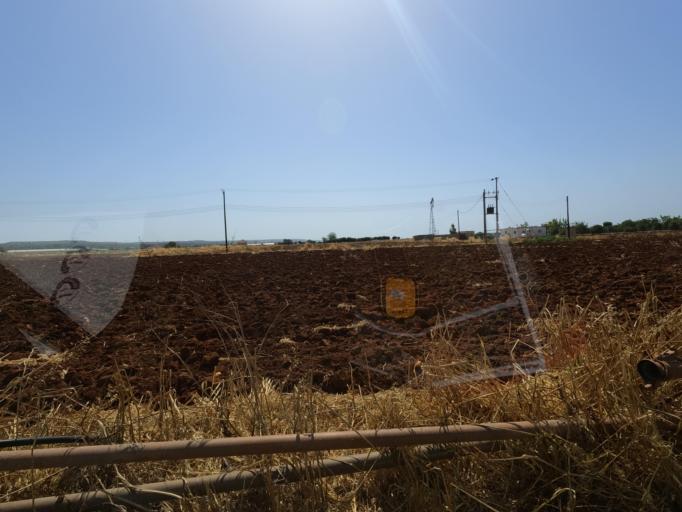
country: CY
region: Ammochostos
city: Frenaros
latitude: 34.9970
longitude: 33.9423
